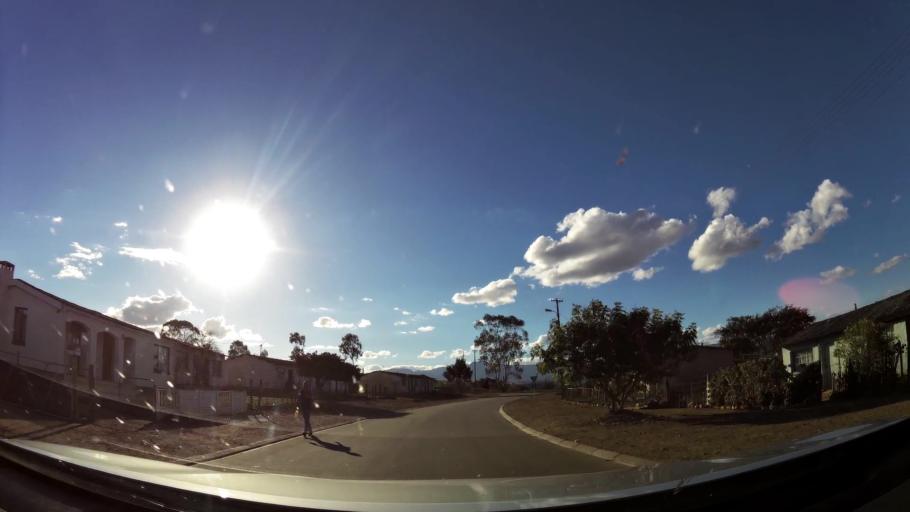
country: ZA
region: Western Cape
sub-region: Eden District Municipality
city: Riversdale
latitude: -34.1023
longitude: 20.9657
